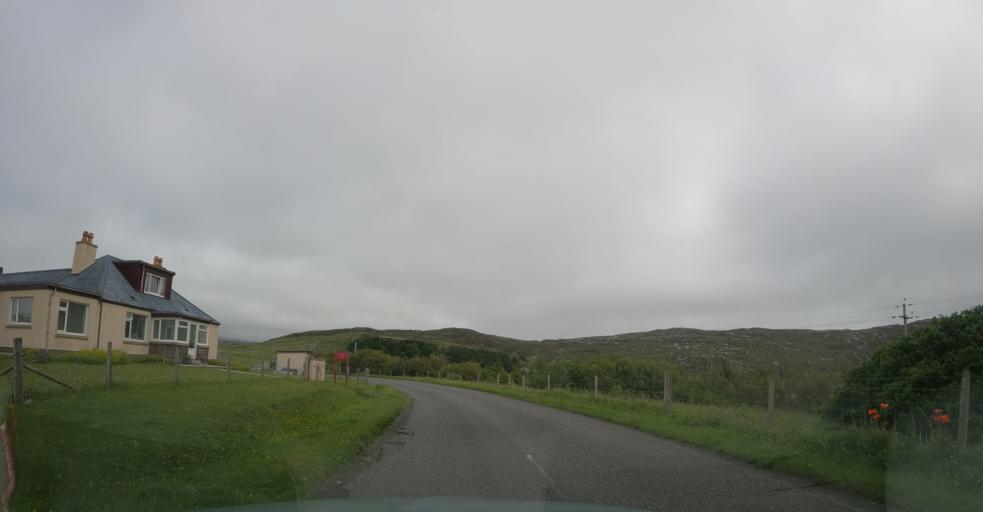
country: GB
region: Scotland
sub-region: Eilean Siar
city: Harris
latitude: 57.8611
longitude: -6.9787
